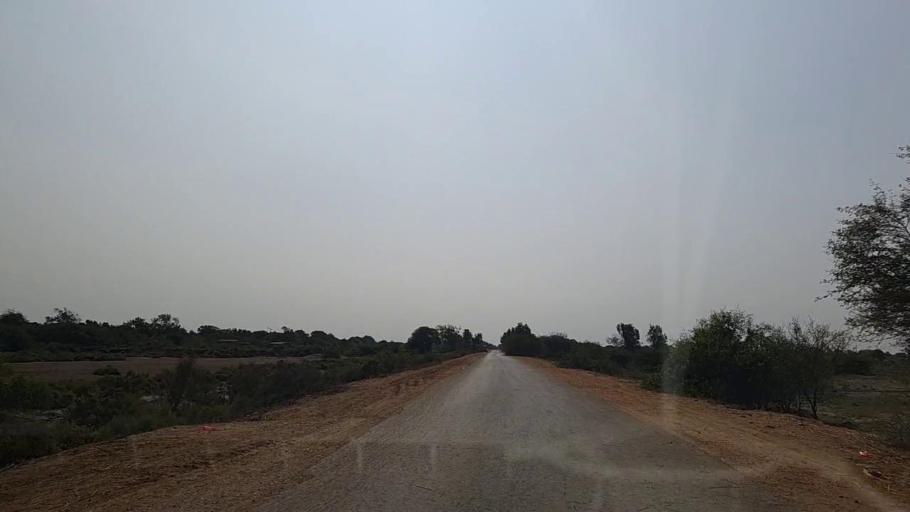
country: PK
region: Sindh
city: Chuhar Jamali
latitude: 24.2597
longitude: 67.9079
